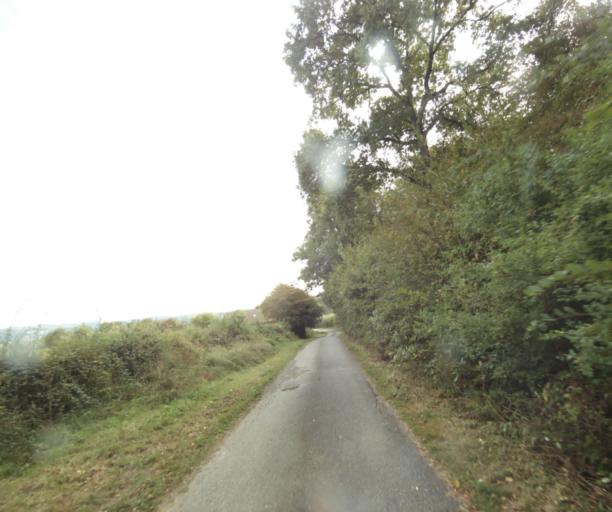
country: FR
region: Bourgogne
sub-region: Departement de Saone-et-Loire
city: Palinges
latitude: 46.5245
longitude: 4.2461
